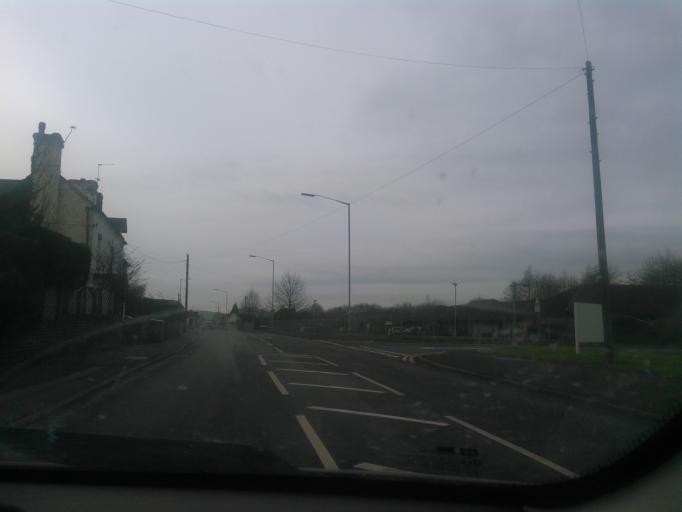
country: GB
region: England
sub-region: Telford and Wrekin
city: Oakengates
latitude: 52.7184
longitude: -2.4437
